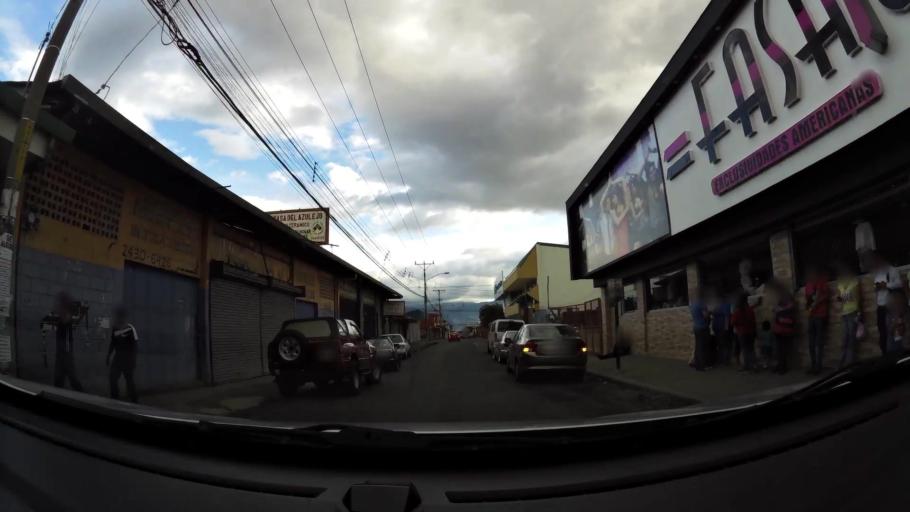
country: CR
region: Alajuela
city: Alajuela
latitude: 10.0143
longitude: -84.2164
